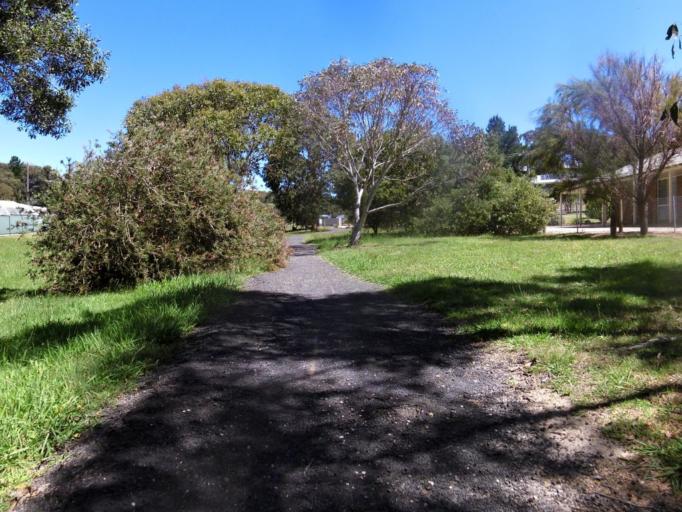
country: AU
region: Victoria
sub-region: Whittlesea
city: Whittlesea
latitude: -37.3620
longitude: 145.0351
